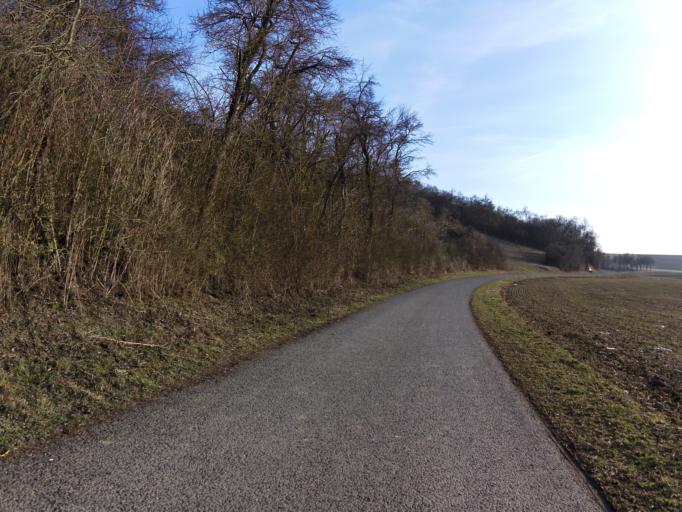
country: DE
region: Bavaria
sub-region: Regierungsbezirk Unterfranken
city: Kurnach
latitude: 49.8396
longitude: 10.0237
